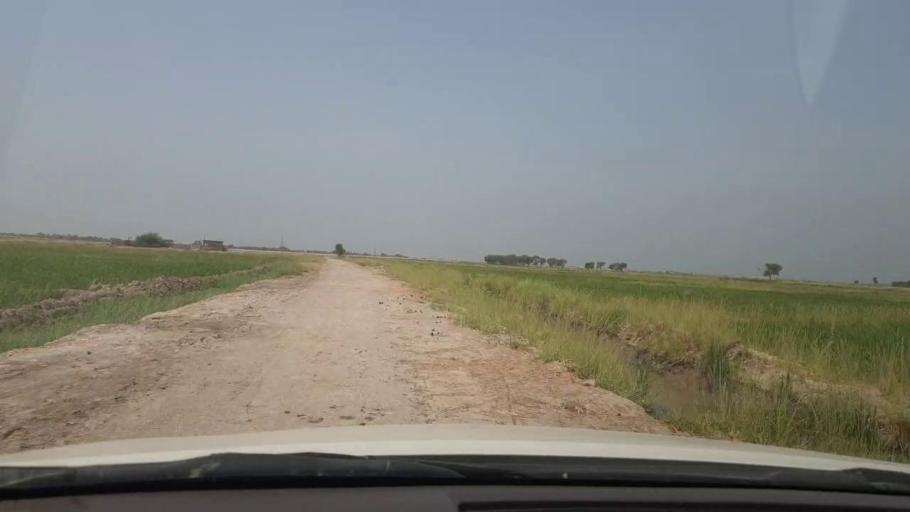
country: PK
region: Sindh
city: Shikarpur
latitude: 28.0239
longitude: 68.6089
